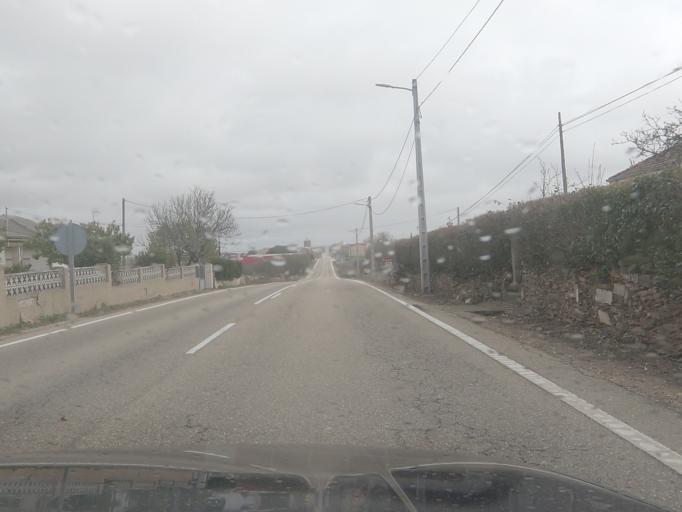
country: ES
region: Castille and Leon
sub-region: Provincia de Zamora
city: Tabara
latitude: 41.8320
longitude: -5.9669
